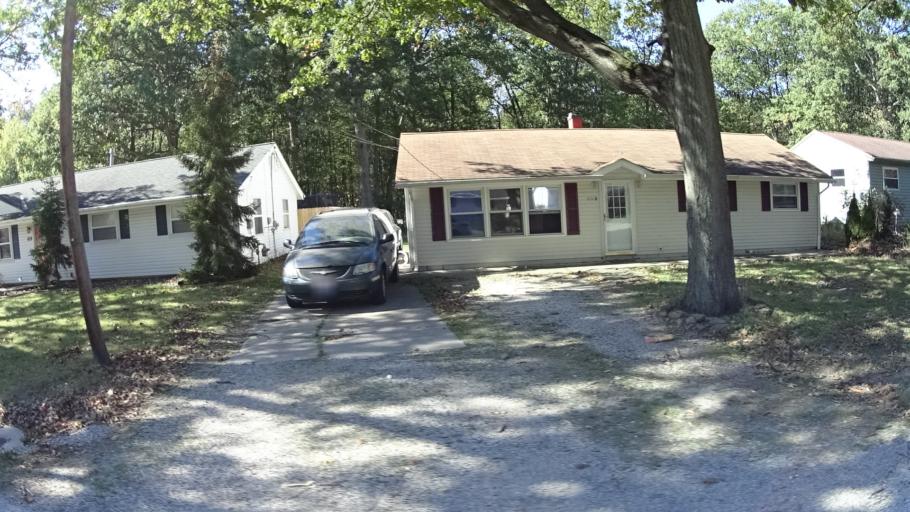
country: US
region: Ohio
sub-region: Lorain County
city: Vermilion-on-the-Lake
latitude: 41.4219
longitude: -82.3256
